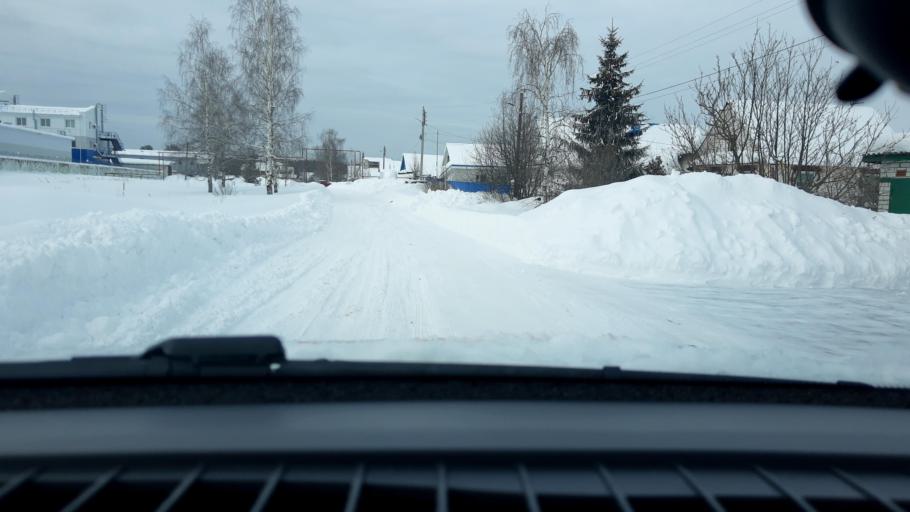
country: RU
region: Nizjnij Novgorod
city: Lukino
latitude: 56.3965
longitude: 43.6999
